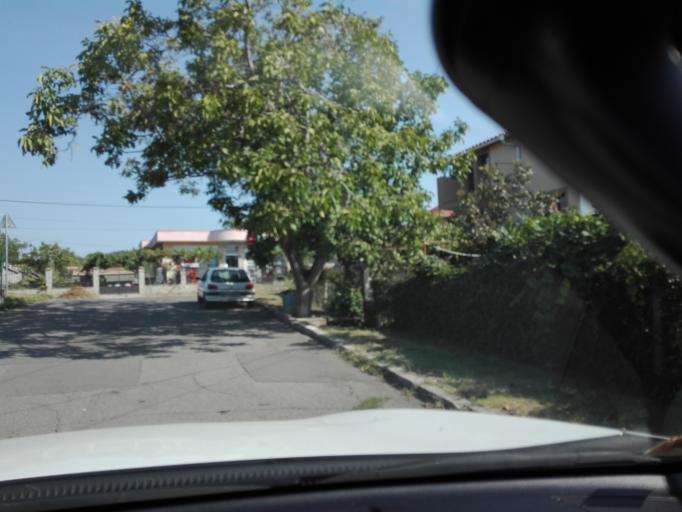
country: BG
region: Burgas
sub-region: Obshtina Kameno
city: Kameno
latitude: 42.6271
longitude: 27.3919
